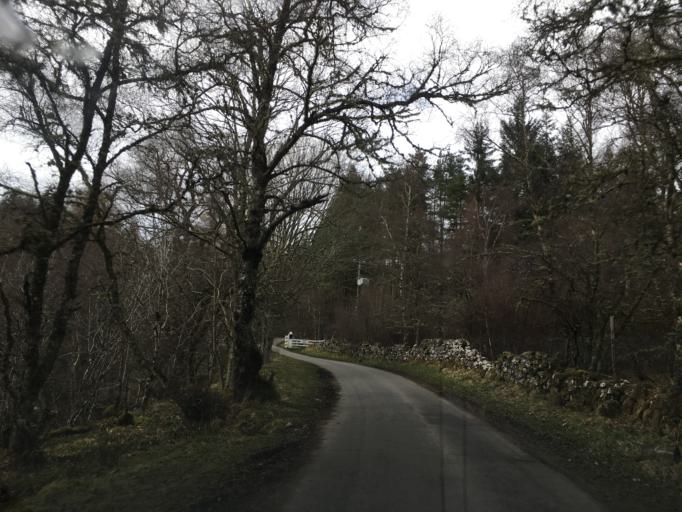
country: GB
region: Scotland
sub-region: Highland
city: Kingussie
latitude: 57.0871
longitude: -4.0543
